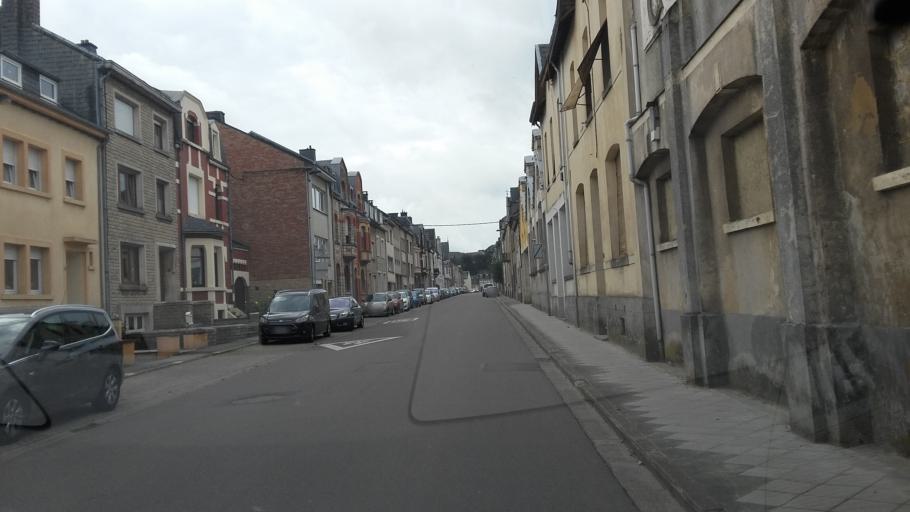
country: BE
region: Wallonia
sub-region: Province du Luxembourg
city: Arlon
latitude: 49.6890
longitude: 5.8067
